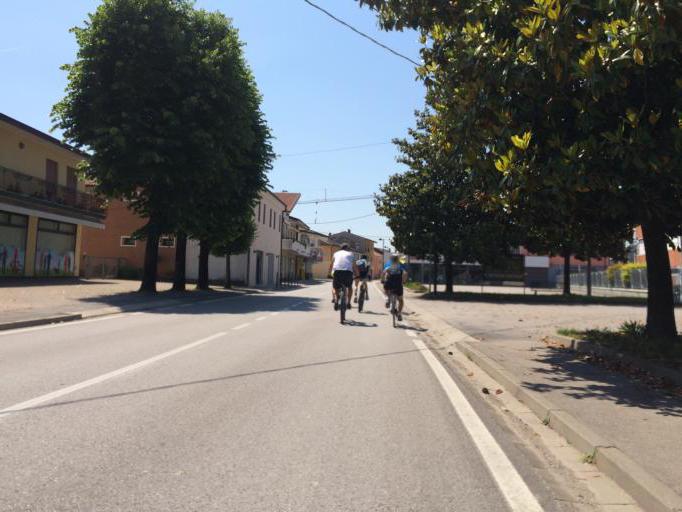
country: IT
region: Veneto
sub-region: Provincia di Vicenza
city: Villaganzerla
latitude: 45.4376
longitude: 11.6173
